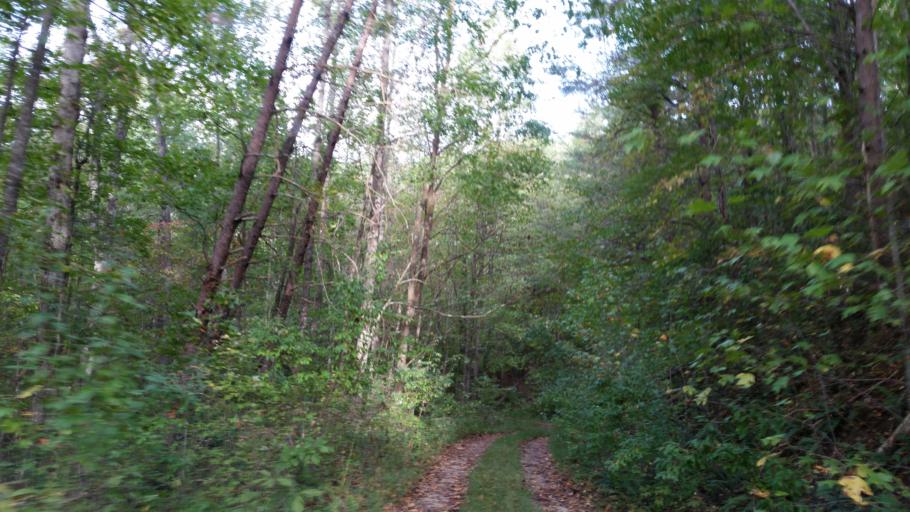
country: US
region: Georgia
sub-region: Dawson County
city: Dawsonville
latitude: 34.5835
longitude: -84.1773
